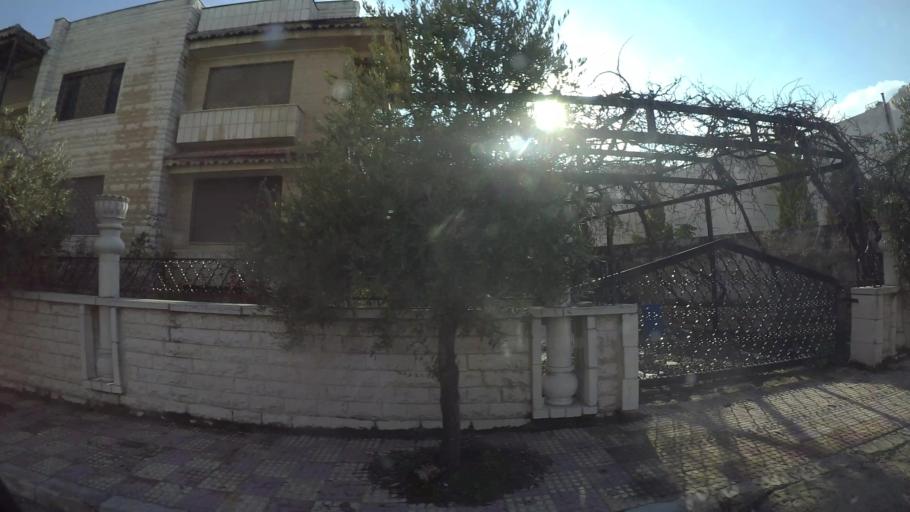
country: JO
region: Amman
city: Al Jubayhah
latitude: 32.0124
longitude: 35.8623
